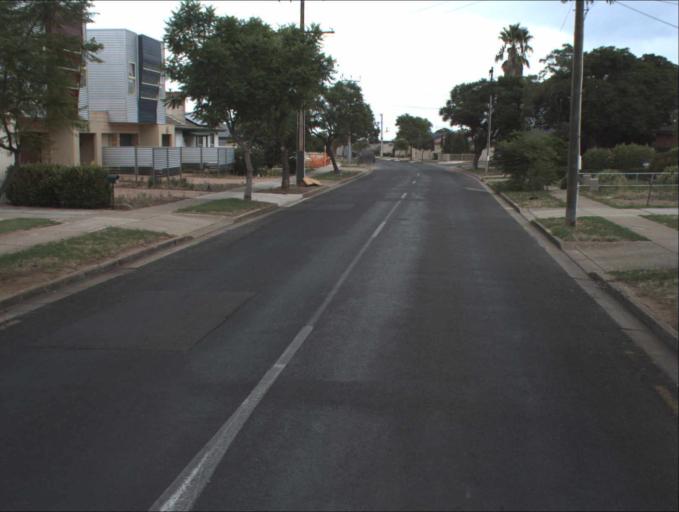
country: AU
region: South Australia
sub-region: Port Adelaide Enfield
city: Enfield
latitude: -34.8552
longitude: 138.6229
